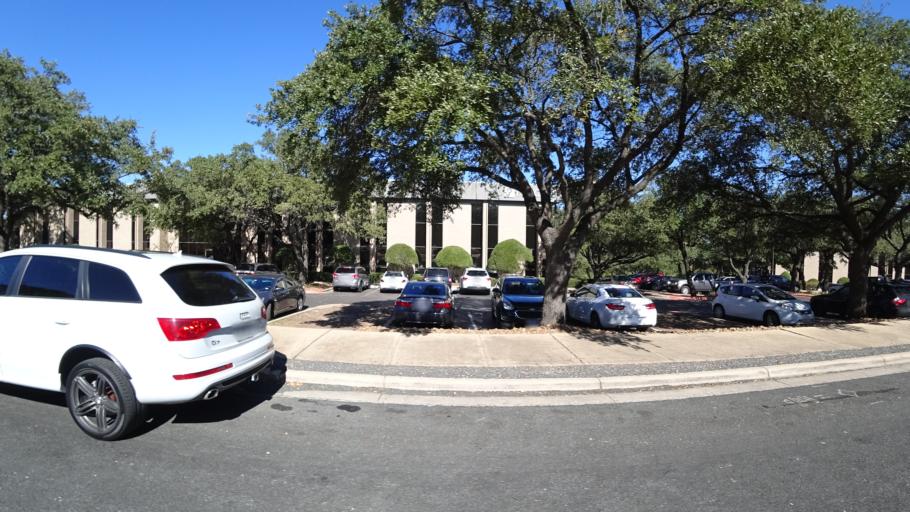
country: US
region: Texas
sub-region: Travis County
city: West Lake Hills
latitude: 30.3625
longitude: -97.7496
